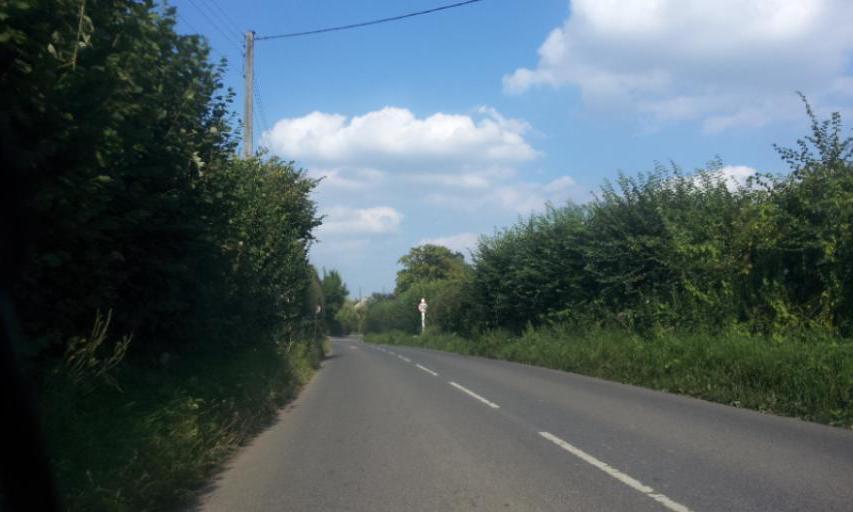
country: GB
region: England
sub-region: Kent
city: Yalding
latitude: 51.2167
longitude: 0.4564
